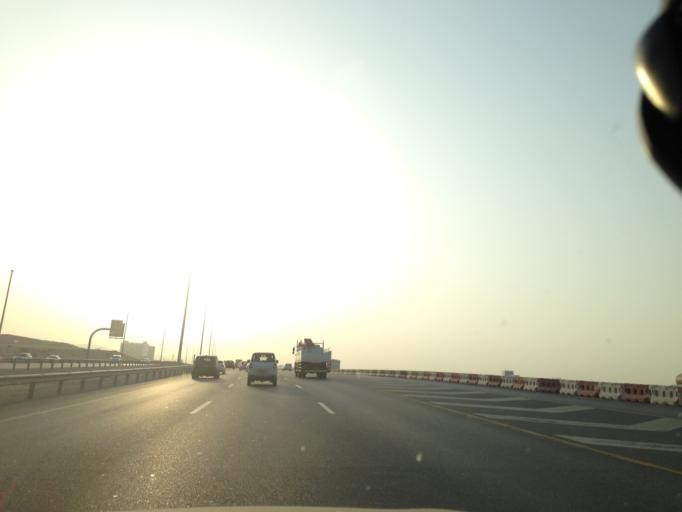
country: OM
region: Muhafazat Masqat
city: Bawshar
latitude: 23.5676
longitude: 58.3729
